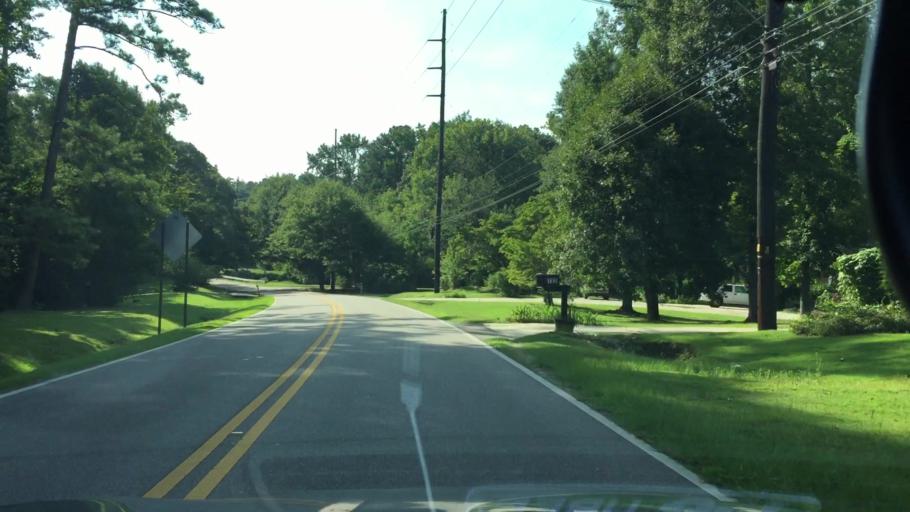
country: US
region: Alabama
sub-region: Lee County
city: Auburn
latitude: 32.5929
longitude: -85.4668
